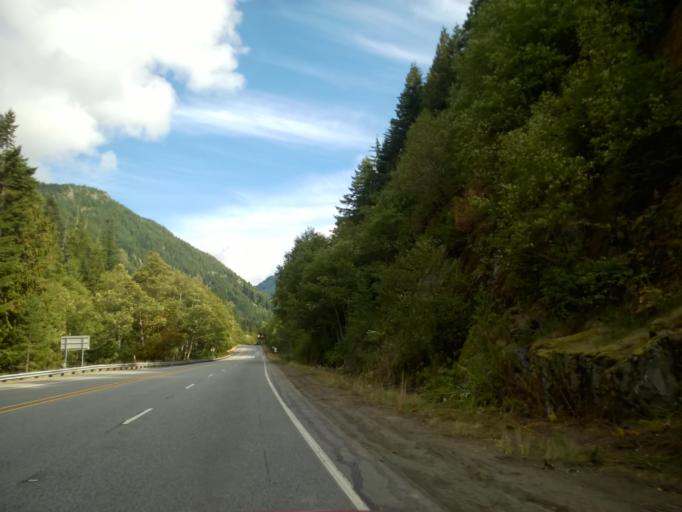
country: US
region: Washington
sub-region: Snohomish County
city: Gold Bar
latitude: 47.7157
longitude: -121.1841
